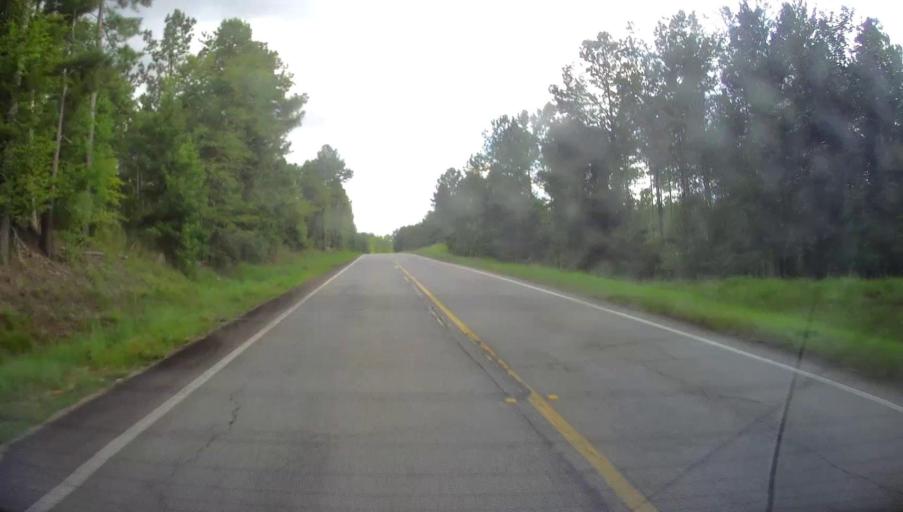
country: US
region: Georgia
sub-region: Crawford County
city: Roberta
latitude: 32.8195
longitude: -84.0223
